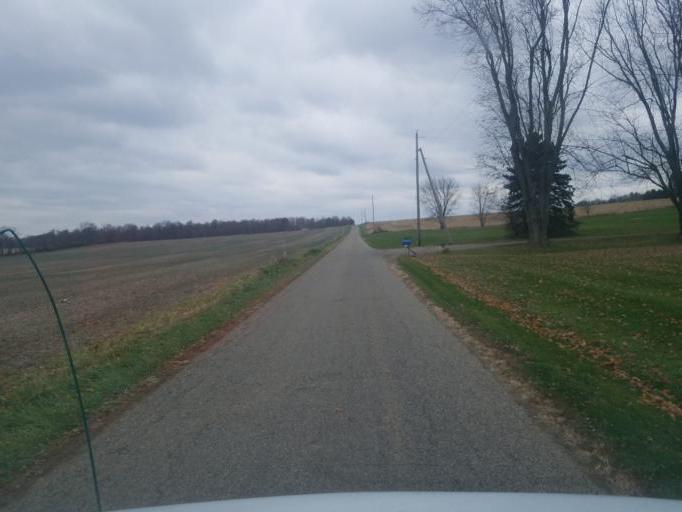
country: US
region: Ohio
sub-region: Knox County
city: Fredericktown
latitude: 40.4768
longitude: -82.5108
